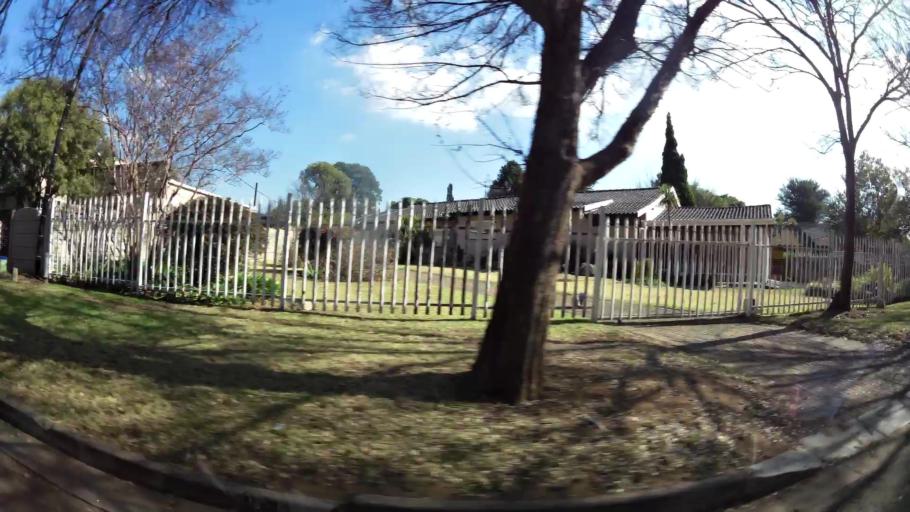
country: ZA
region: Gauteng
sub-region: Ekurhuleni Metropolitan Municipality
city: Benoni
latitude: -26.1432
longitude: 28.3469
